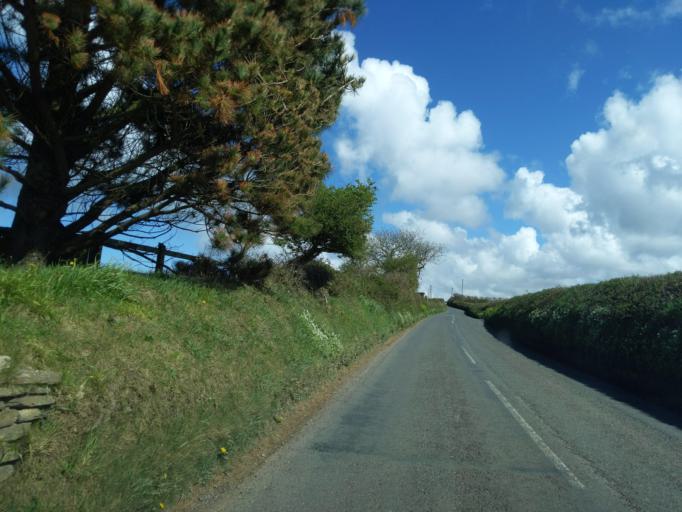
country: GB
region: England
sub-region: Cornwall
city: Wadebridge
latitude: 50.5736
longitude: -4.8377
